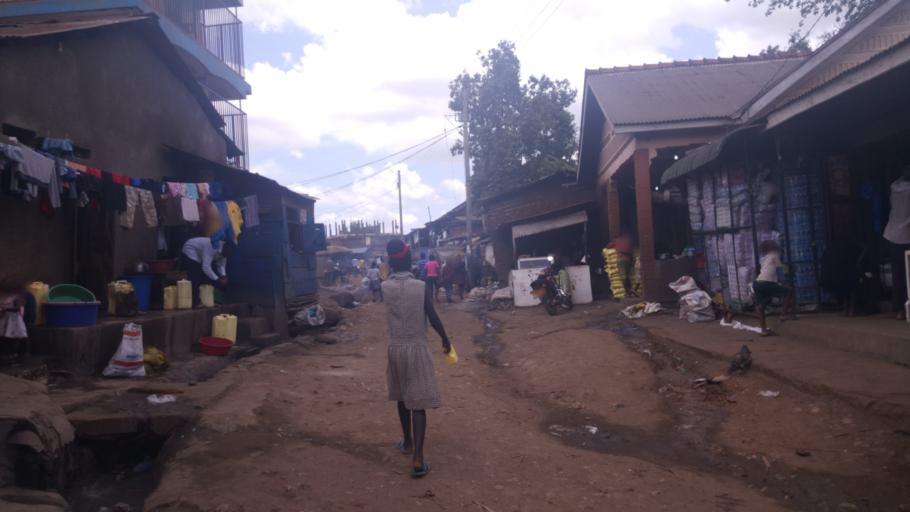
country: UG
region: Central Region
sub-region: Kampala District
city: Kampala
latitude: 0.3042
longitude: 32.5795
